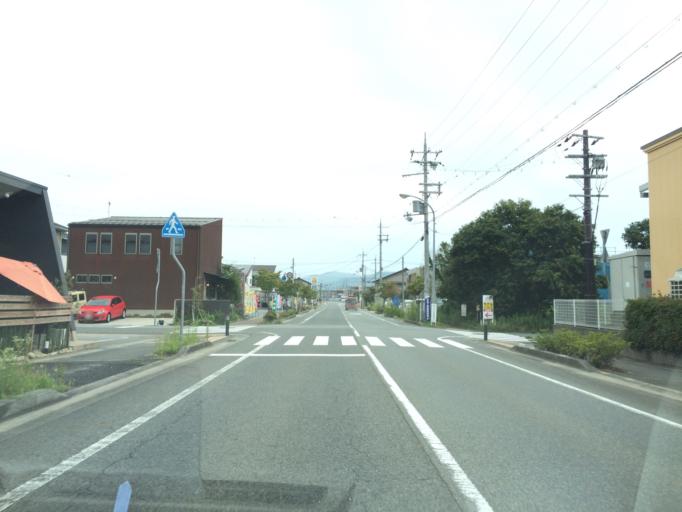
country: JP
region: Hyogo
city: Toyooka
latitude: 35.5392
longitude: 134.8092
